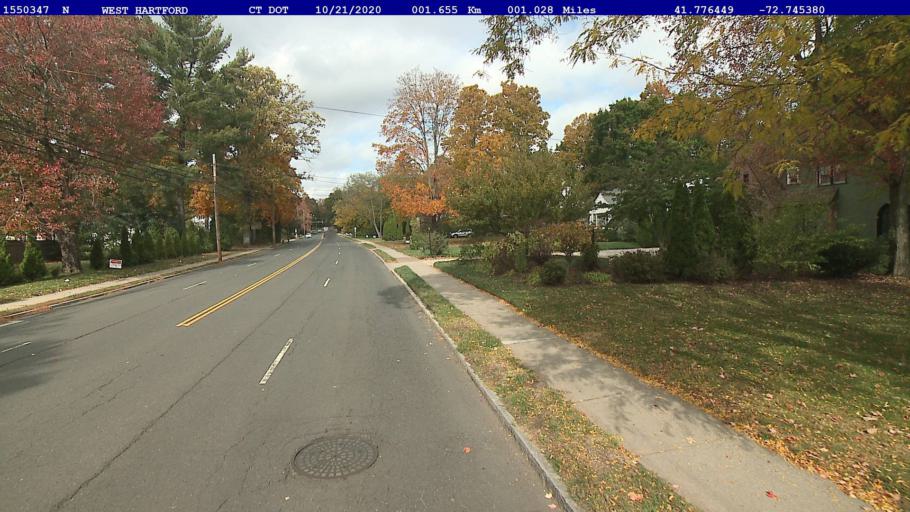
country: US
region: Connecticut
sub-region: Hartford County
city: West Hartford
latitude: 41.7765
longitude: -72.7454
